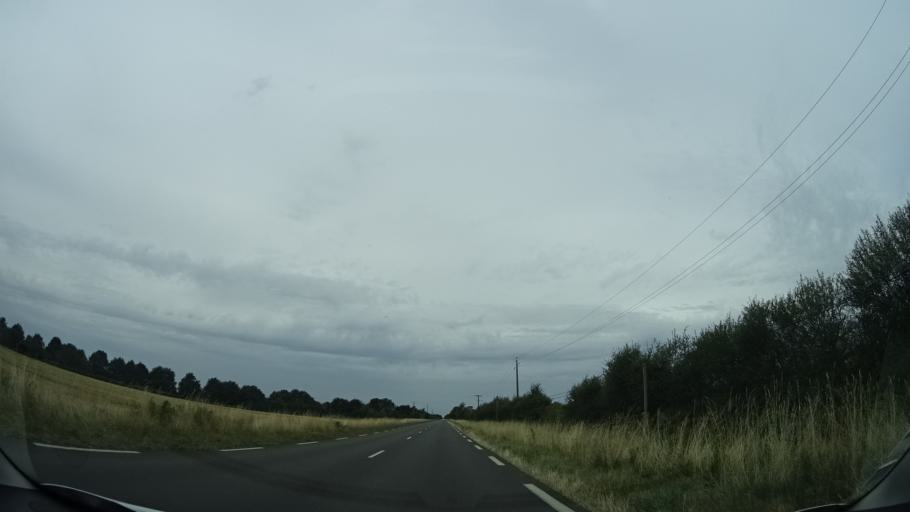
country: FR
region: Pays de la Loire
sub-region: Departement de la Mayenne
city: Meslay-du-Maine
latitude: 47.9714
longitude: -0.5933
